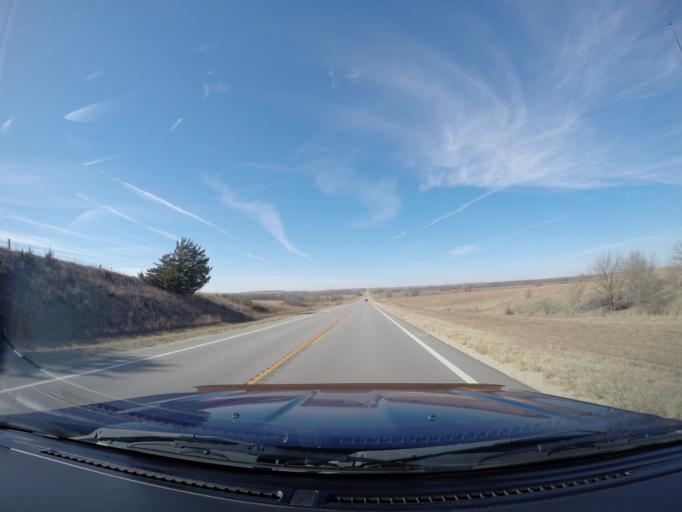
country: US
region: Kansas
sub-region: Cloud County
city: Concordia
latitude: 39.3647
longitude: -97.6371
